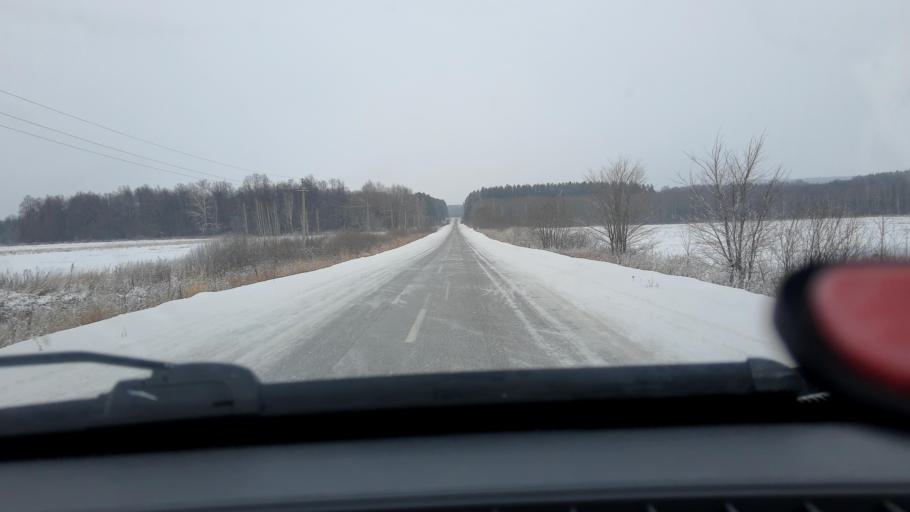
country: RU
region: Bashkortostan
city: Iglino
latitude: 54.6689
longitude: 56.4211
